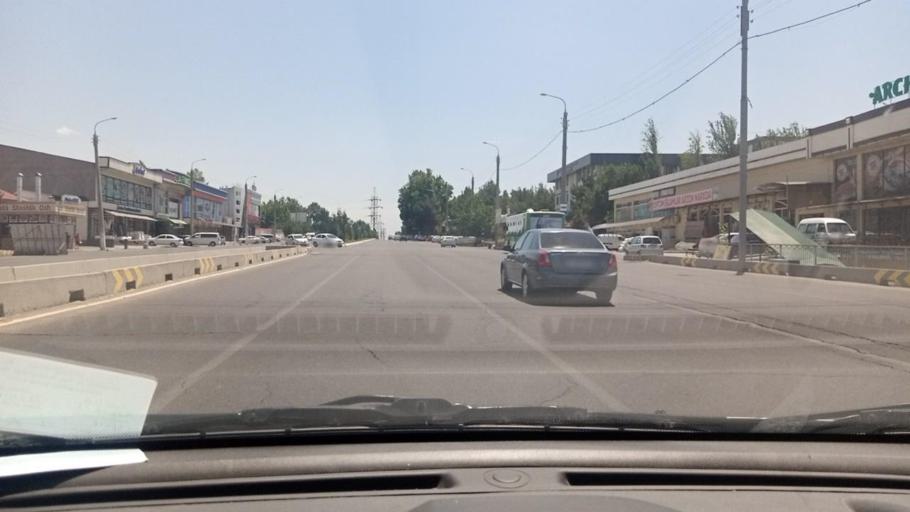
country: UZ
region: Toshkent Shahri
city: Tashkent
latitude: 41.3027
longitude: 69.1937
